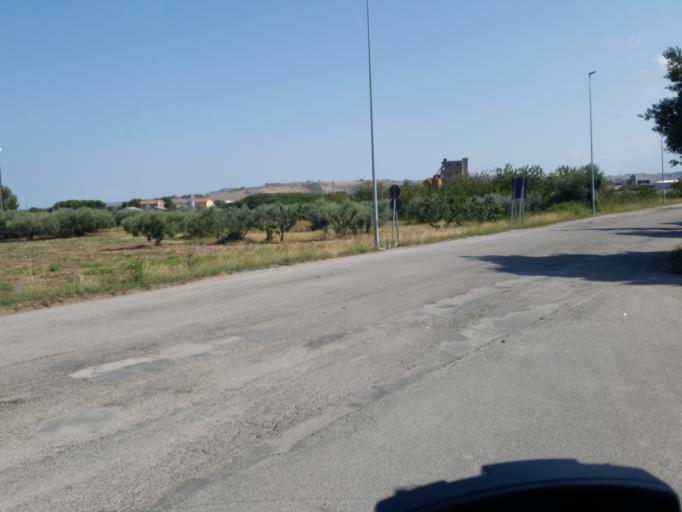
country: IT
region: Abruzzo
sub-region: Provincia di Chieti
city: Salvo Marina
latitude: 42.0655
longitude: 14.7616
